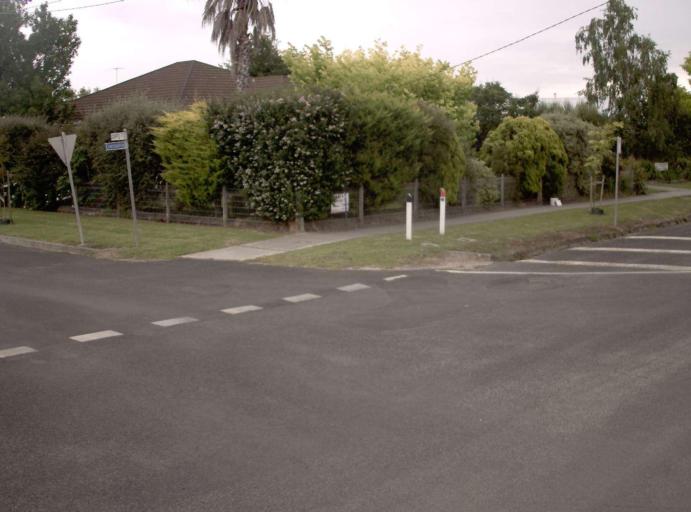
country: AU
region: Victoria
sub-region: Latrobe
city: Traralgon
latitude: -38.5593
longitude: 146.6769
